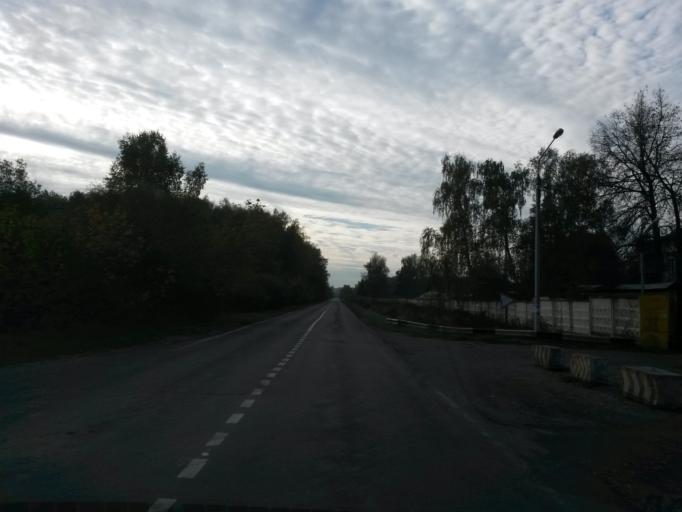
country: RU
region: Moskovskaya
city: Melikhovo
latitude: 55.2083
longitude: 37.6918
